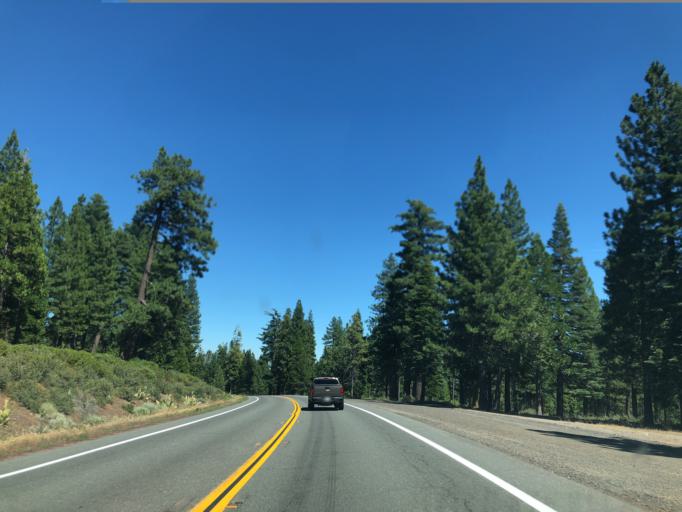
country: US
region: California
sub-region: Lassen County
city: Susanville
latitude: 40.4262
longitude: -120.8113
